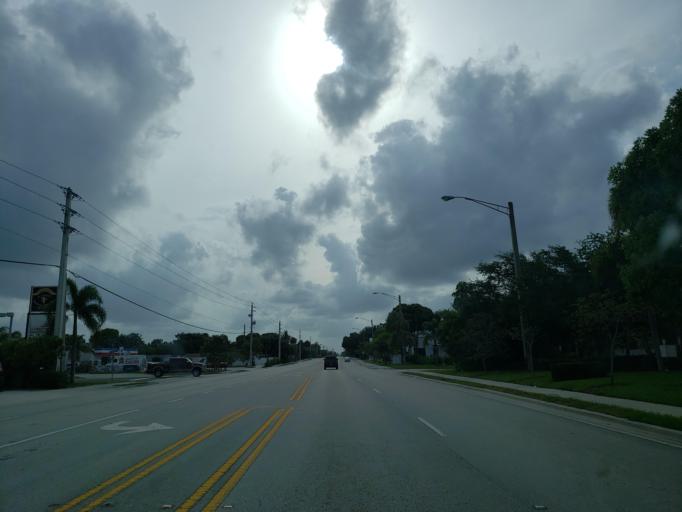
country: US
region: Florida
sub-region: Martin County
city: Sewall's Point
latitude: 27.1975
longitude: -80.2274
